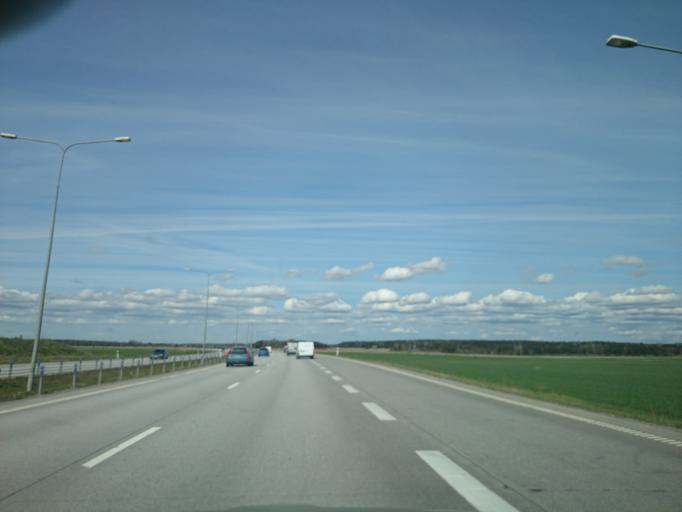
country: SE
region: Uppsala
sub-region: Uppsala Kommun
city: Saevja
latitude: 59.8486
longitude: 17.7344
